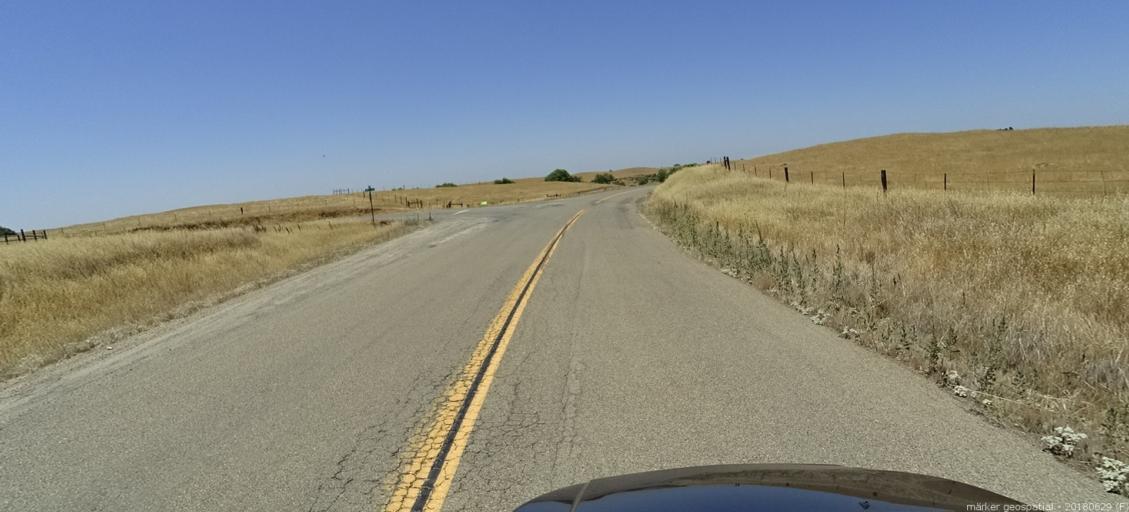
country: US
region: California
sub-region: Madera County
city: Bonadelle Ranchos-Madera Ranchos
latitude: 37.0809
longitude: -119.8864
